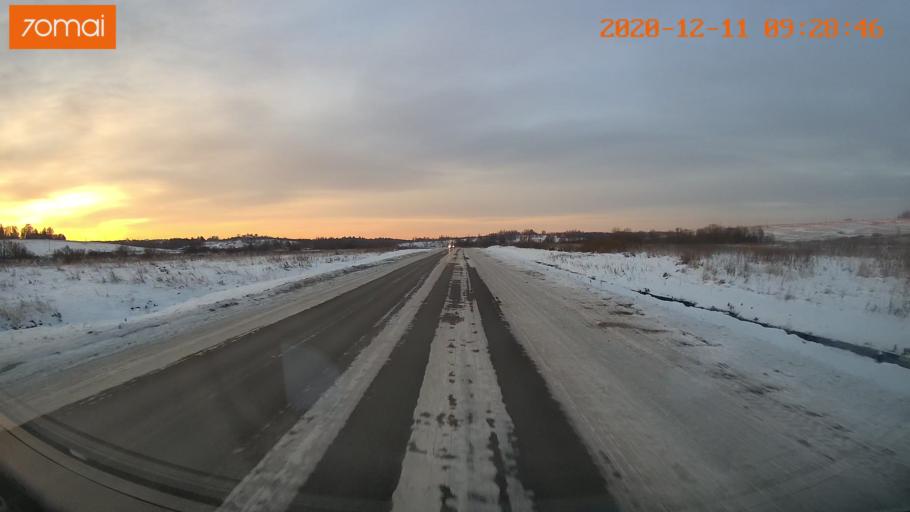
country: RU
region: Vologda
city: Vologda
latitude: 59.1496
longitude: 40.0061
